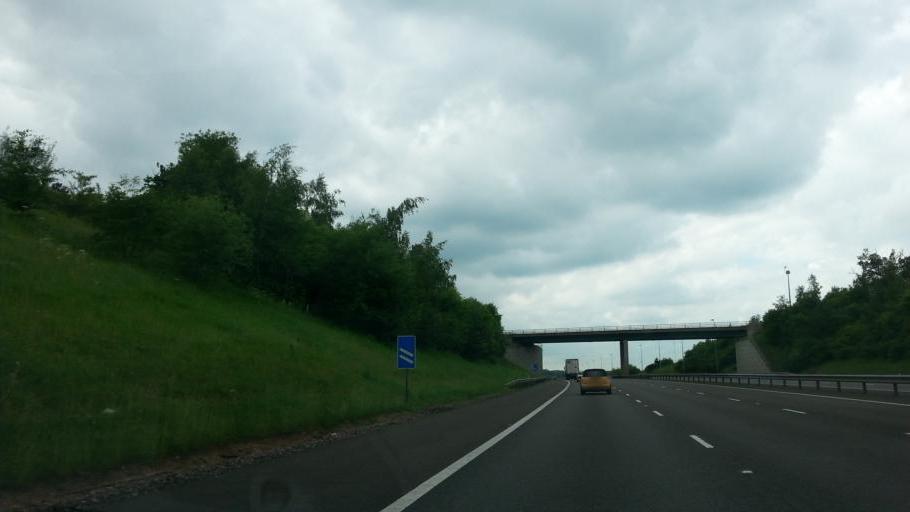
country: GB
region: England
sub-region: Warwickshire
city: Curdworth
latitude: 52.5628
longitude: -1.7573
